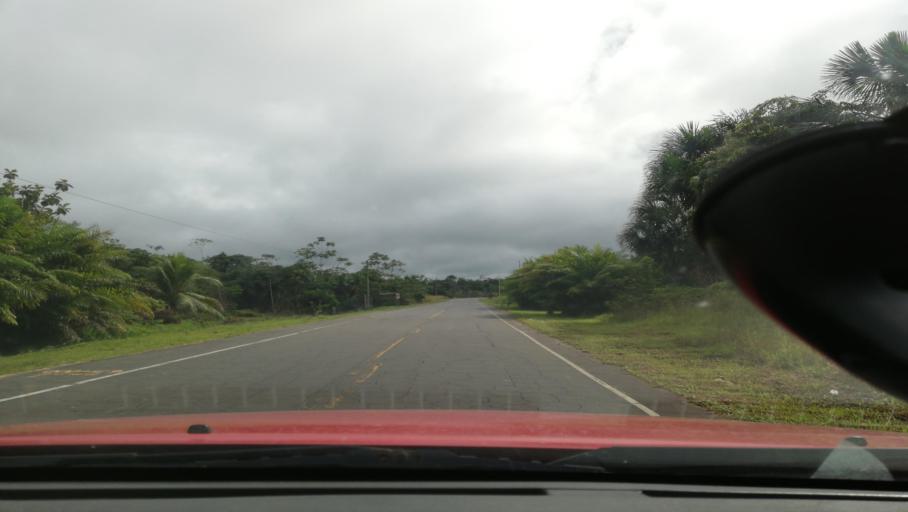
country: PE
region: Loreto
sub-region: Provincia de Loreto
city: Nauta
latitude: -4.2892
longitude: -73.5173
